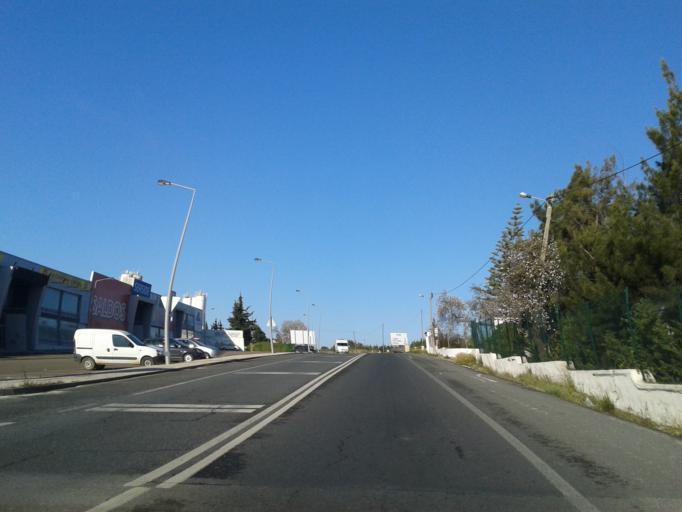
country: PT
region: Faro
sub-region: Silves
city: Armacao de Pera
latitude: 37.1313
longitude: -8.3491
